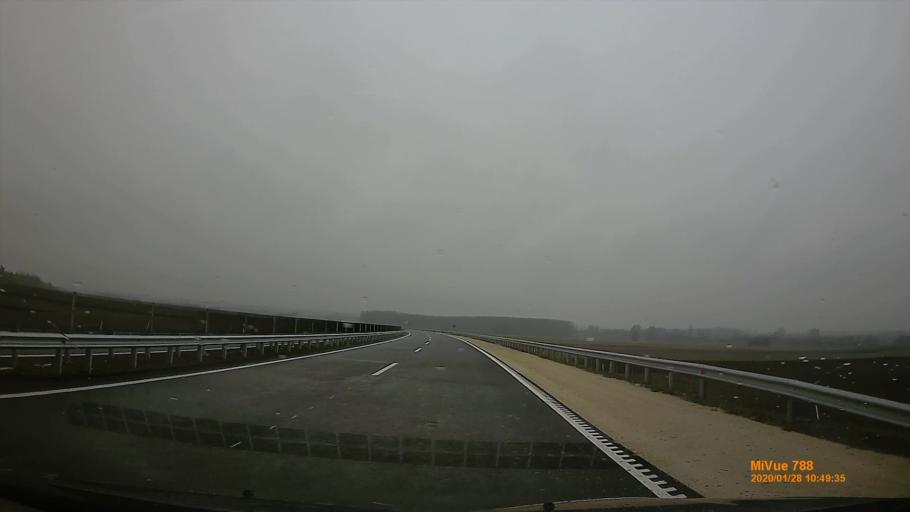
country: HU
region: Pest
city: Monor
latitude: 47.3808
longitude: 19.4439
